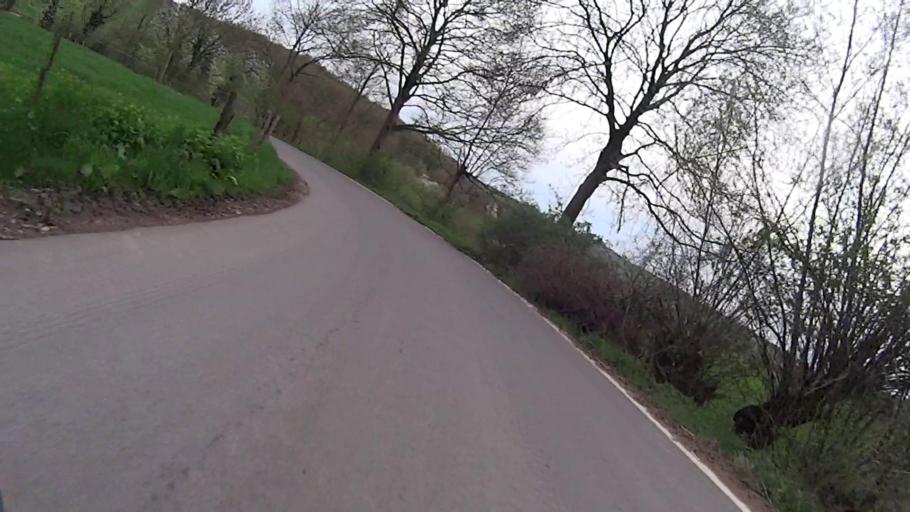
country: BE
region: Flanders
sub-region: Provincie Limburg
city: Sint-Pieters-Voeren
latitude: 50.7570
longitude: 5.8249
